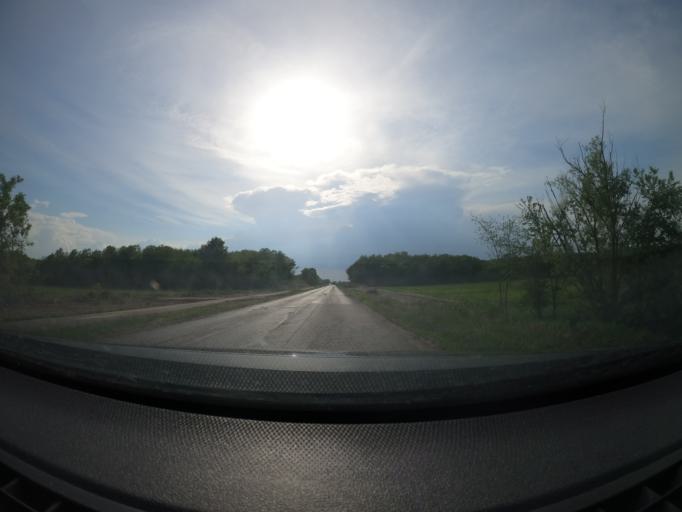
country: HU
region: Hajdu-Bihar
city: Vamospercs
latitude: 47.5266
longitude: 21.9324
